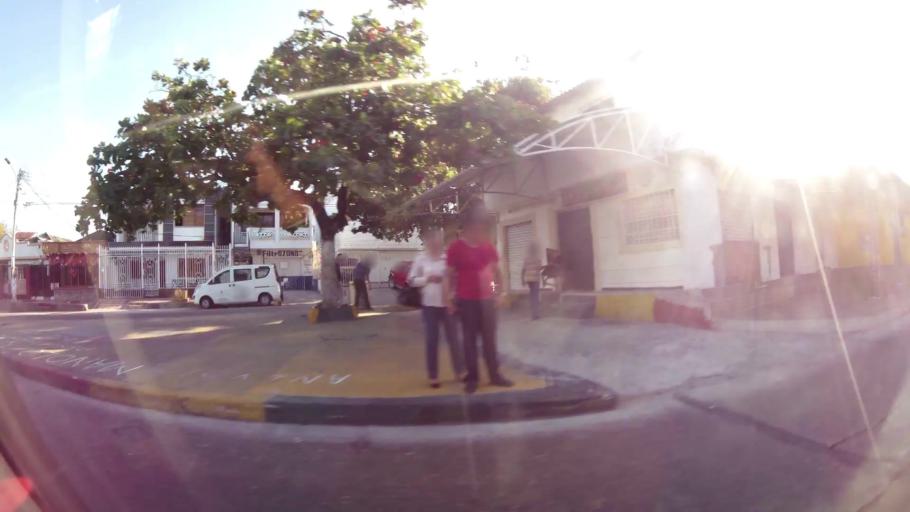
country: CO
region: Atlantico
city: Barranquilla
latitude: 10.9888
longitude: -74.7987
